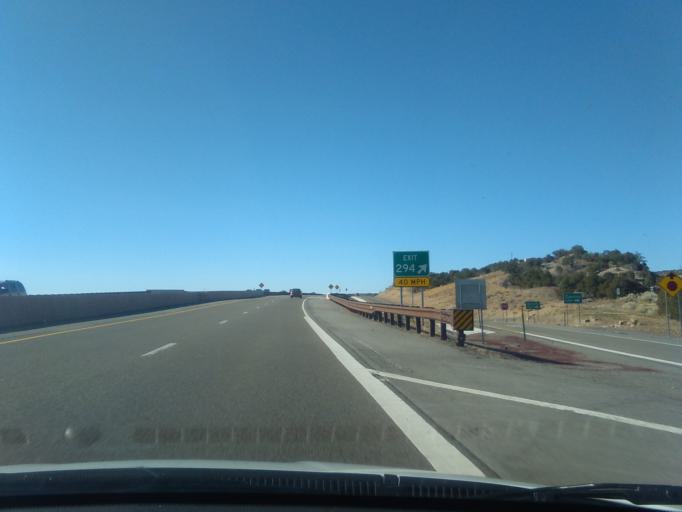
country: US
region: New Mexico
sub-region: Santa Fe County
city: Eldorado at Santa Fe
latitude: 35.5486
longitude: -105.8267
